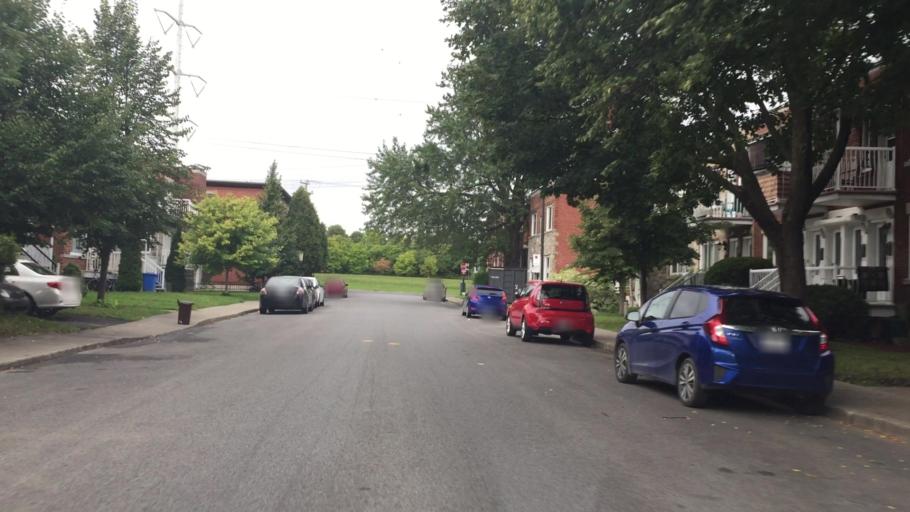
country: CA
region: Quebec
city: Saint-Raymond
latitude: 45.4467
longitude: -73.5879
